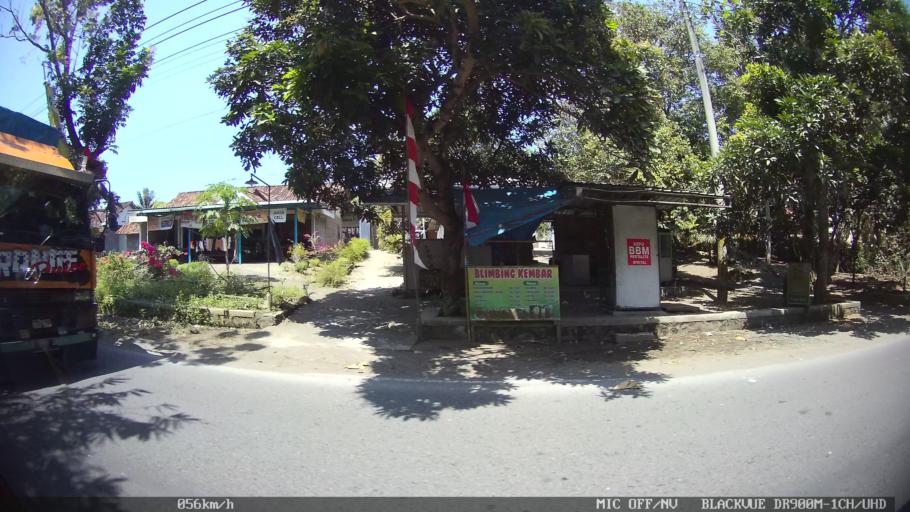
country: ID
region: Daerah Istimewa Yogyakarta
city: Srandakan
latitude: -7.9208
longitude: 110.1125
